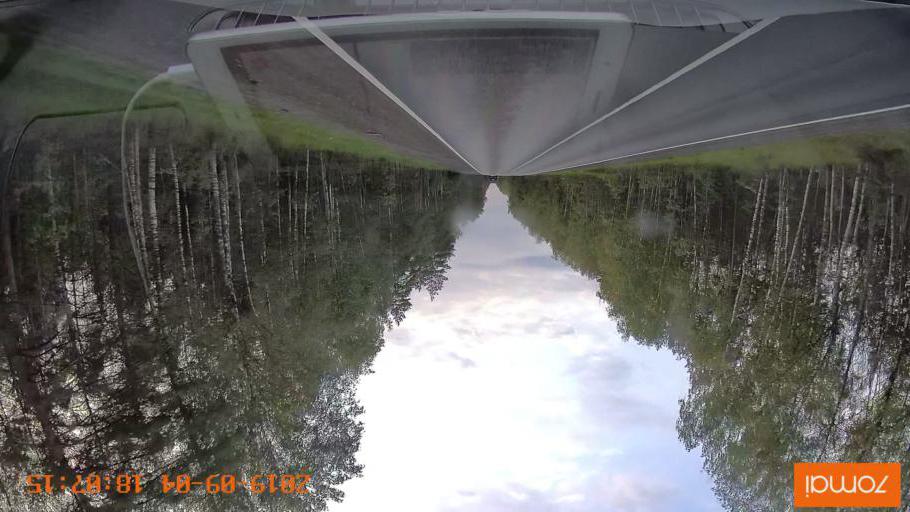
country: RU
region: Moskovskaya
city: Khorlovo
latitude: 55.4213
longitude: 38.8035
